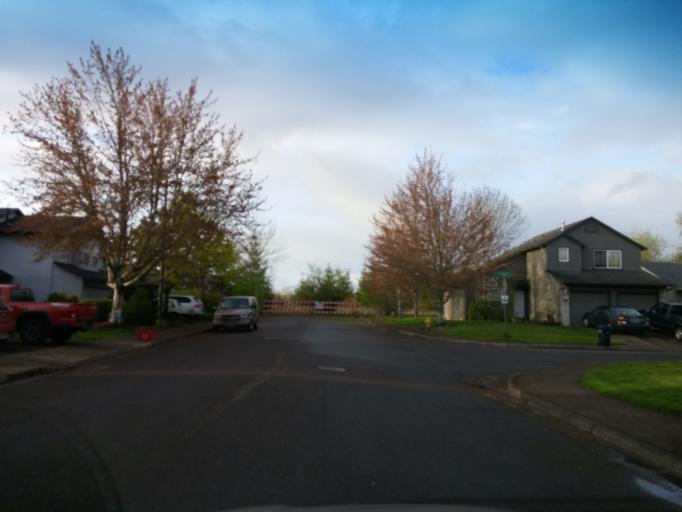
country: US
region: Oregon
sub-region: Washington County
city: Aloha
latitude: 45.5170
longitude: -122.8567
